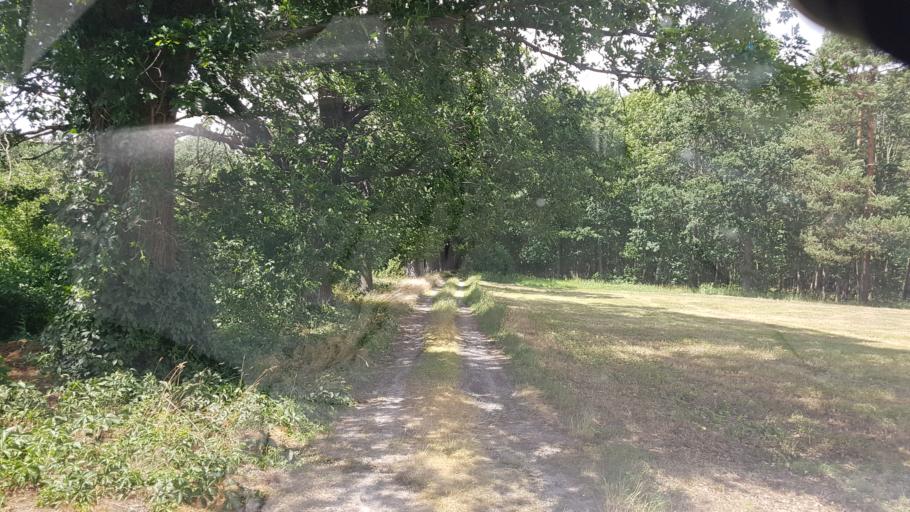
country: DE
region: Brandenburg
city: Sallgast
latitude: 51.5956
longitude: 13.8390
